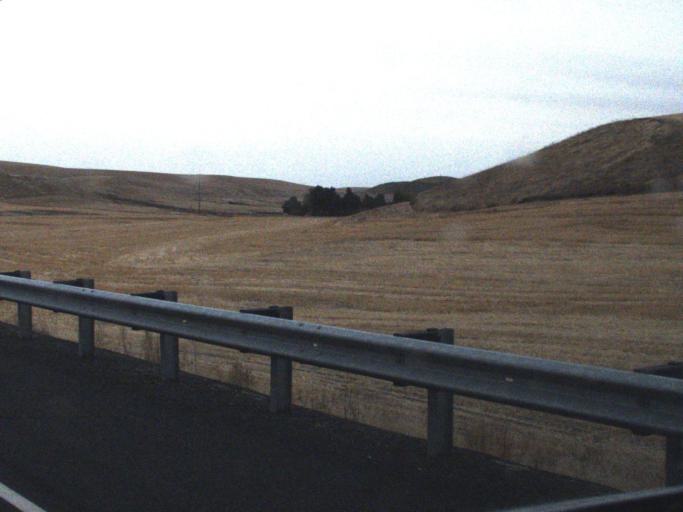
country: US
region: Washington
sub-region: Adams County
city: Ritzville
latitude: 46.7856
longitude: -118.3845
